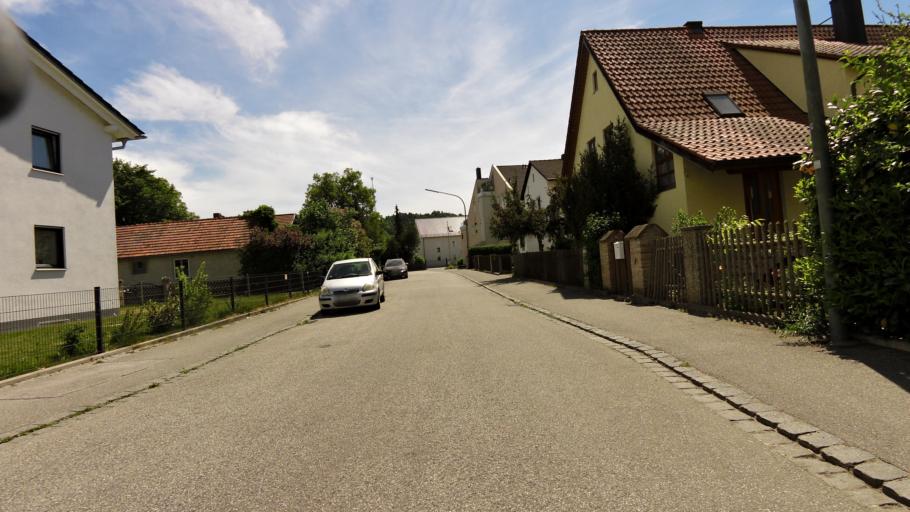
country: DE
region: Bavaria
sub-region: Lower Bavaria
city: Stallwang
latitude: 48.5677
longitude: 12.2055
